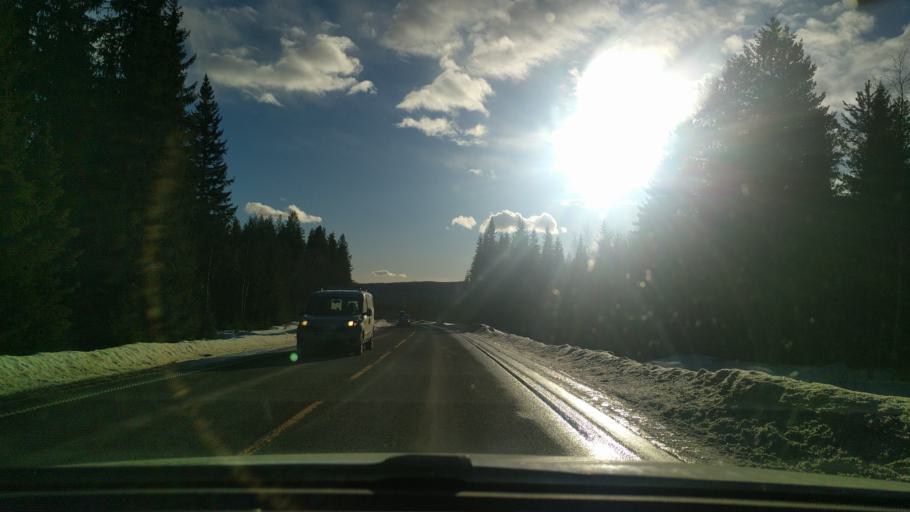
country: NO
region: Hedmark
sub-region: Trysil
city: Innbygda
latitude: 61.1041
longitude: 12.0121
